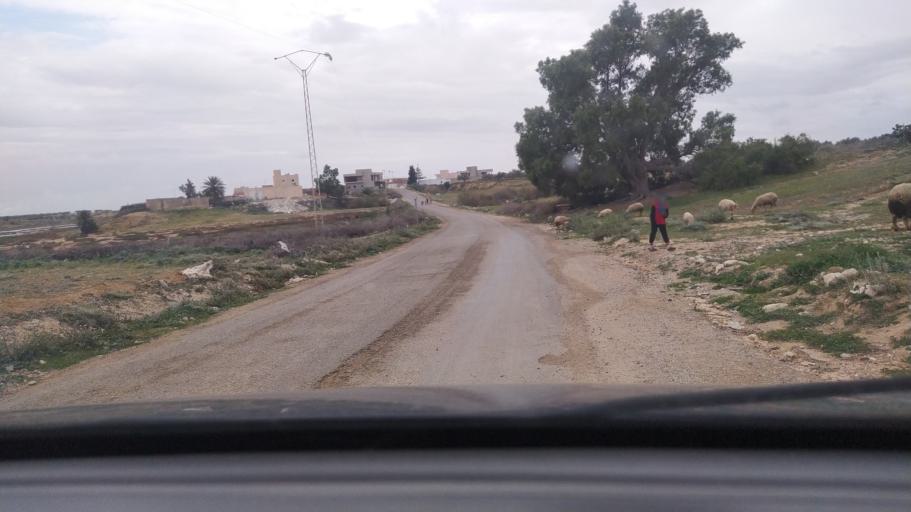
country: TN
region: Al Munastir
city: Sidi Bin Nur
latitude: 35.5177
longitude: 10.9662
